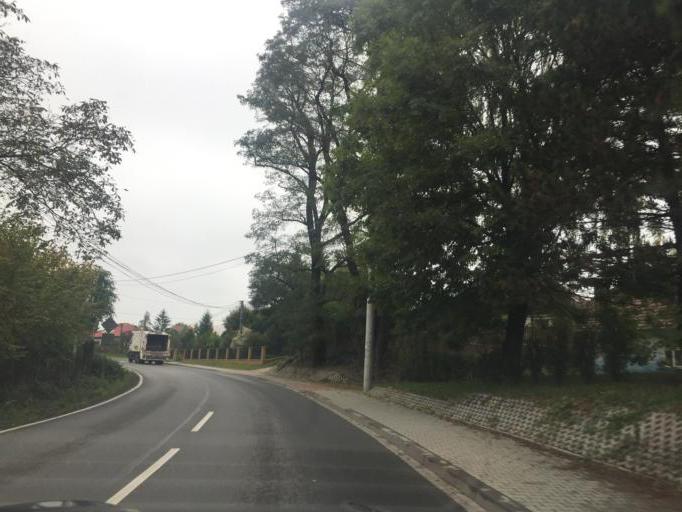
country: PL
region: Lesser Poland Voivodeship
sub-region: Powiat wielicki
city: Wieliczka
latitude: 49.9914
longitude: 20.0247
